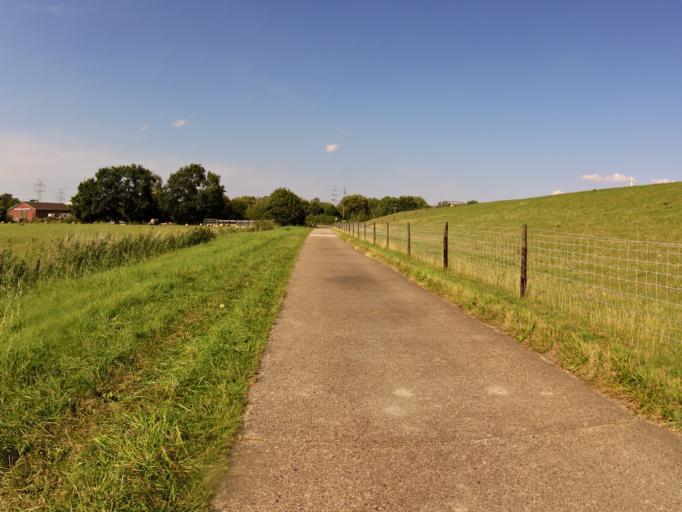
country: DE
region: Lower Saxony
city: Nordenham
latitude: 53.4230
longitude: 8.4719
